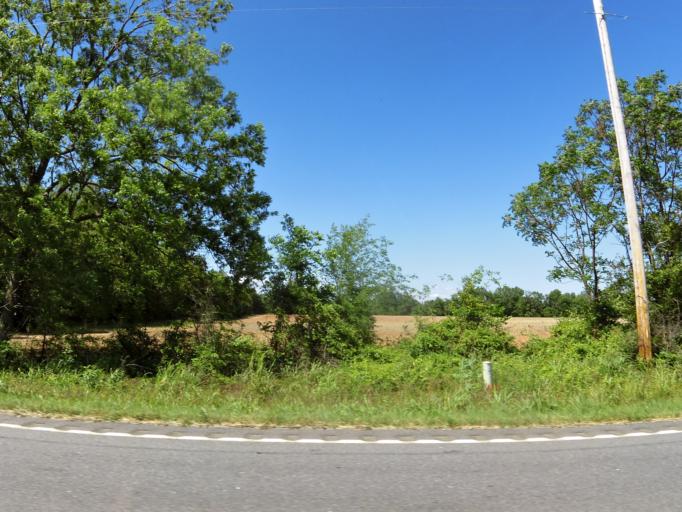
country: US
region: South Carolina
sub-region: Aiken County
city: Aiken
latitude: 33.5233
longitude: -81.6162
